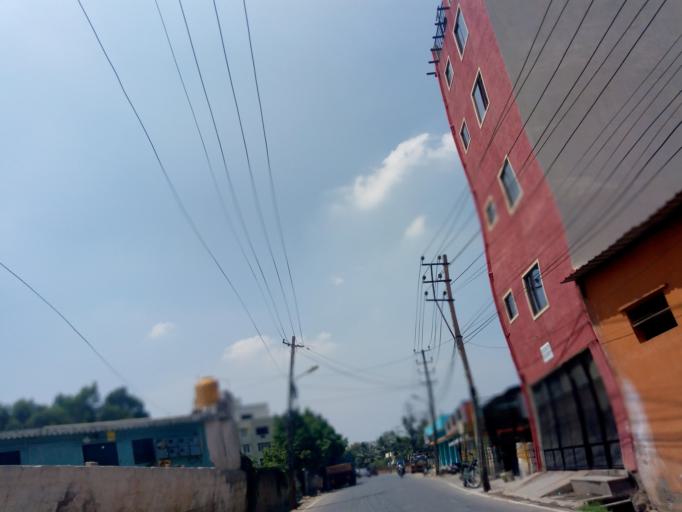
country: IN
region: Karnataka
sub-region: Bangalore Urban
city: Bangalore
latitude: 12.8953
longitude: 77.6509
